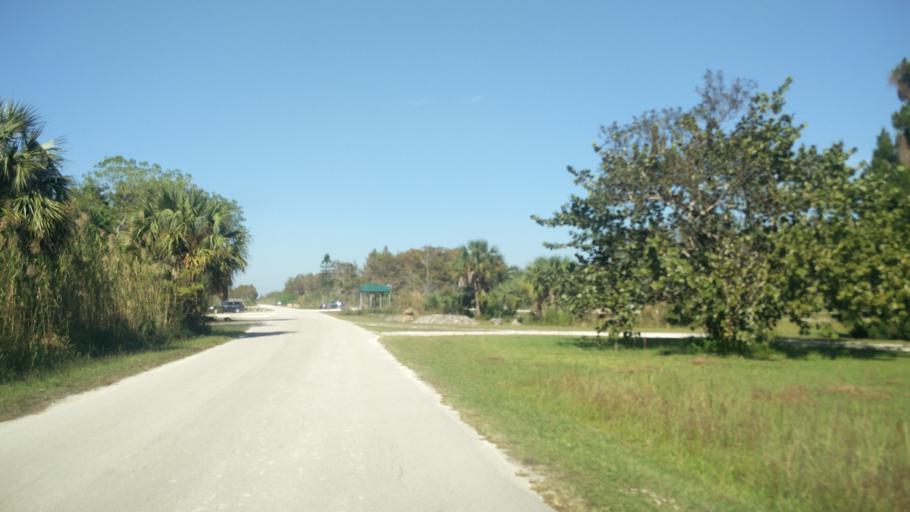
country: US
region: Florida
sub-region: Collier County
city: Lely Resort
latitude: 25.9504
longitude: -81.3605
